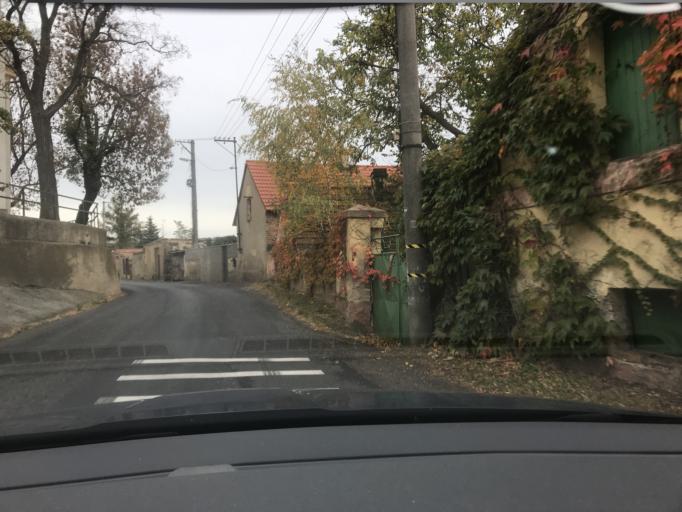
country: CZ
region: Ustecky
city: Libochovice
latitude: 50.4316
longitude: 14.0062
